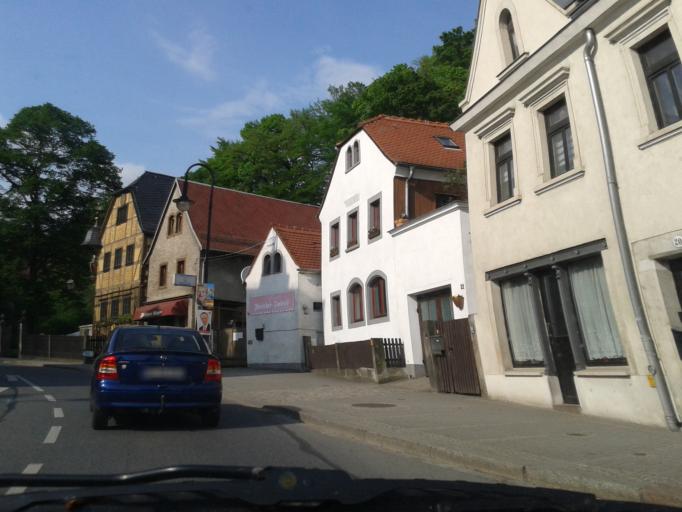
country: DE
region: Saxony
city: Albertstadt
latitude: 51.0546
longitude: 13.8167
